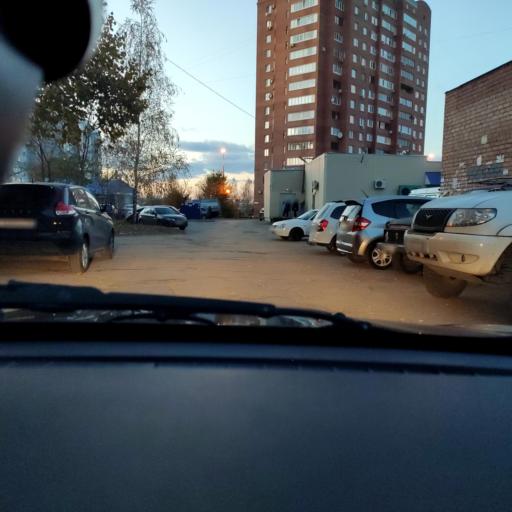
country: RU
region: Samara
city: Tol'yatti
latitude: 53.5466
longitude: 49.3442
